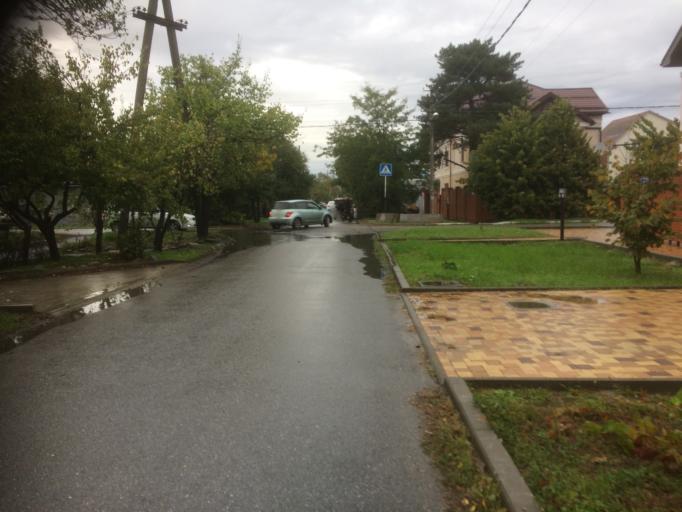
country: RU
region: Krasnodarskiy
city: Krasnodar
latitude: 45.0410
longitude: 38.9382
